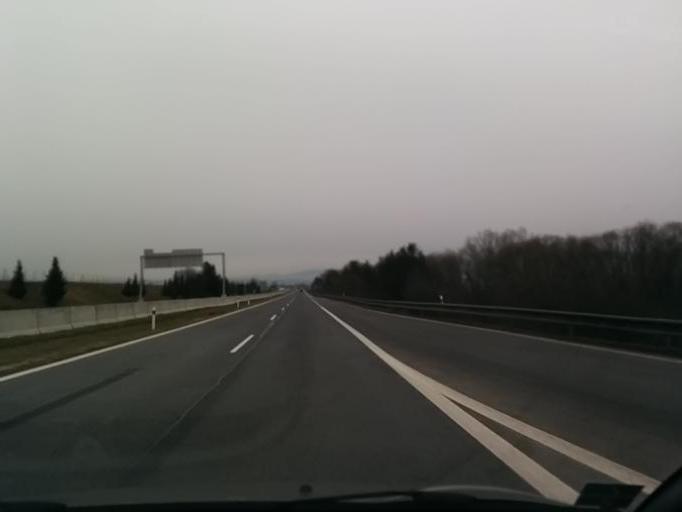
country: SK
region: Banskobystricky
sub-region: Okres Banska Bystrica
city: Zvolen
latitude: 48.5997
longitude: 19.1112
